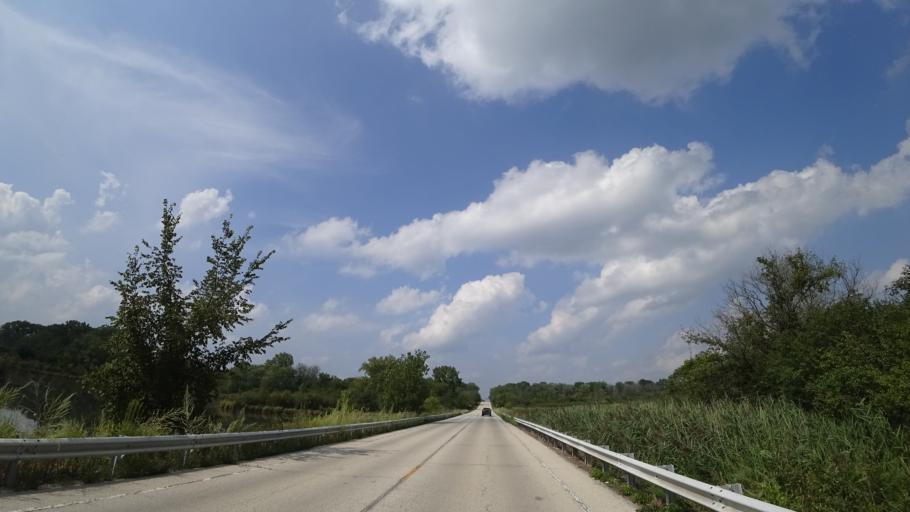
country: US
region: Illinois
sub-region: Will County
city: Goodings Grove
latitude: 41.6601
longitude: -87.9125
